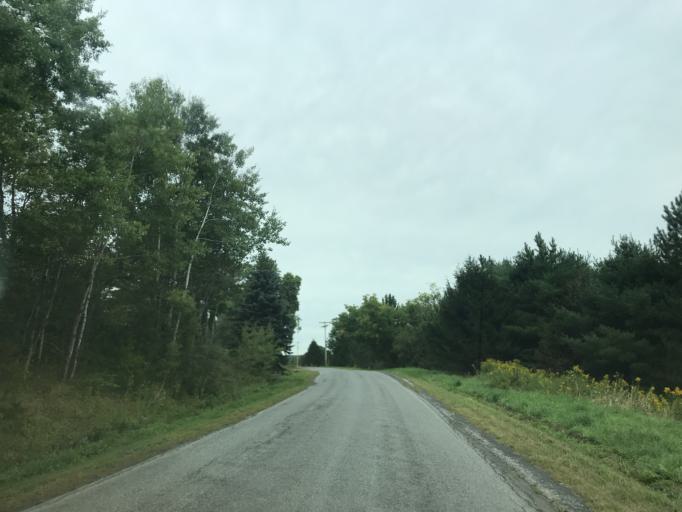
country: US
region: New York
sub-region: Otsego County
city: Worcester
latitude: 42.5541
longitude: -74.6651
